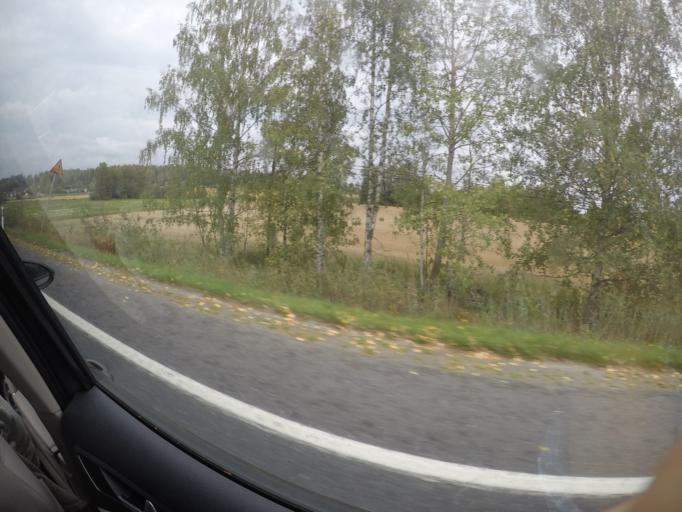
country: FI
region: Haeme
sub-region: Haemeenlinna
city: Parola
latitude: 61.0693
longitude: 24.3920
